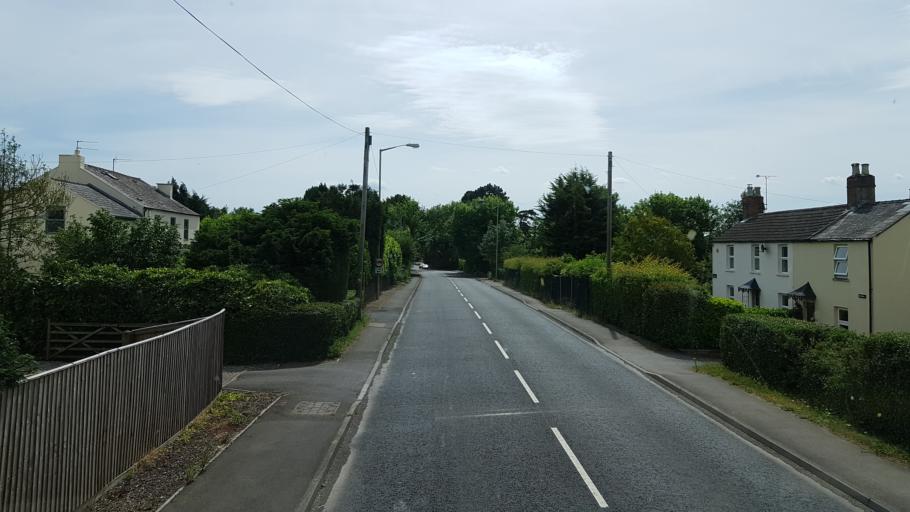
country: GB
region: England
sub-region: Gloucestershire
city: Shurdington
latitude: 51.8708
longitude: -2.1086
